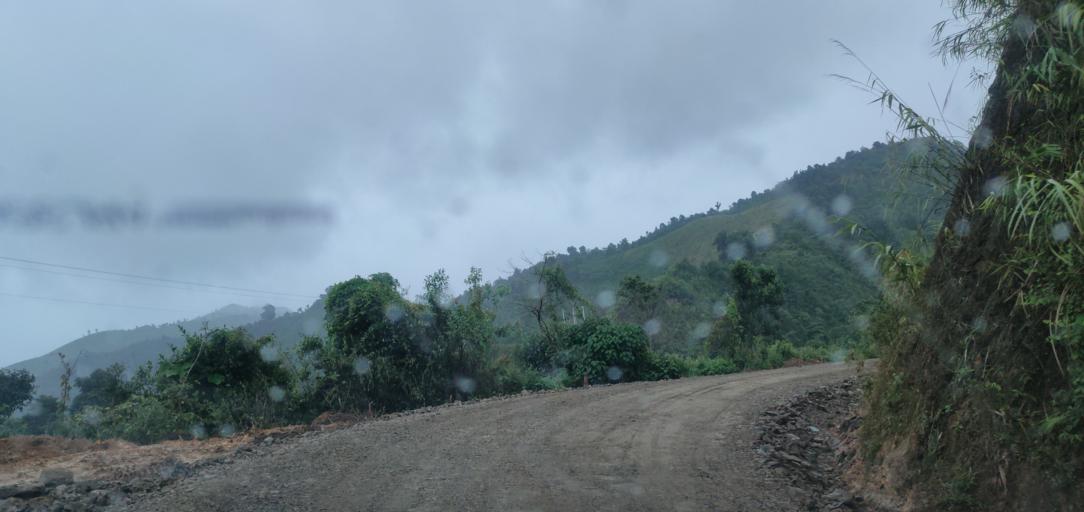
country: LA
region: Phongsali
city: Phongsali
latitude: 21.4317
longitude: 102.1604
